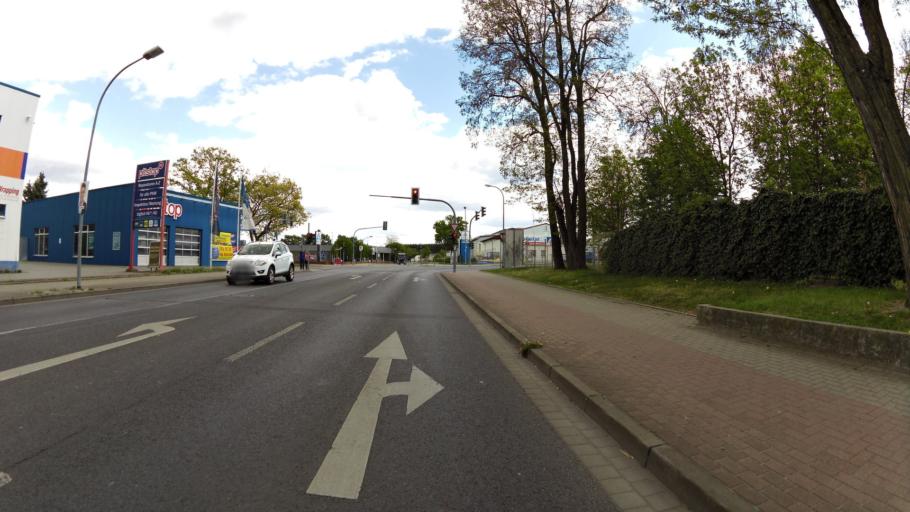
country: DE
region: Brandenburg
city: Furstenwalde
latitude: 52.3663
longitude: 14.0679
